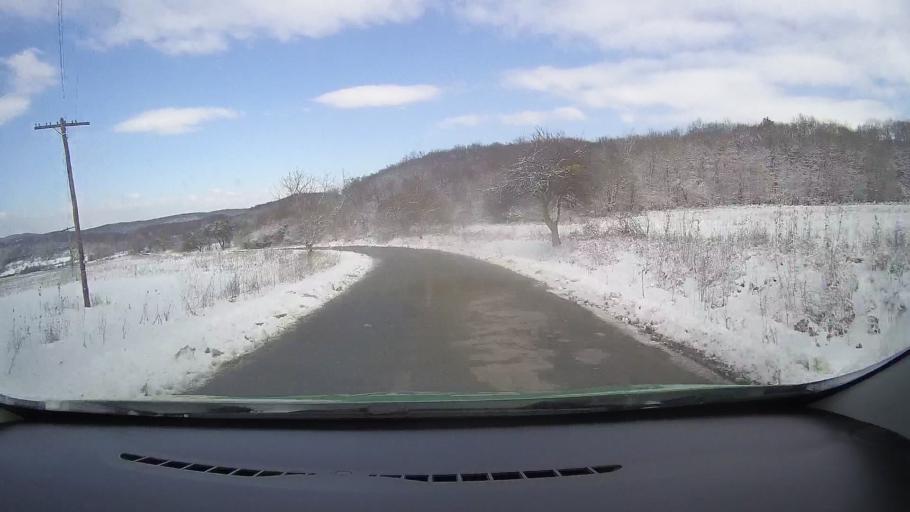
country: RO
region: Sibiu
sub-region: Comuna Mihaileni
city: Mihaileni
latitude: 46.0033
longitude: 24.4259
